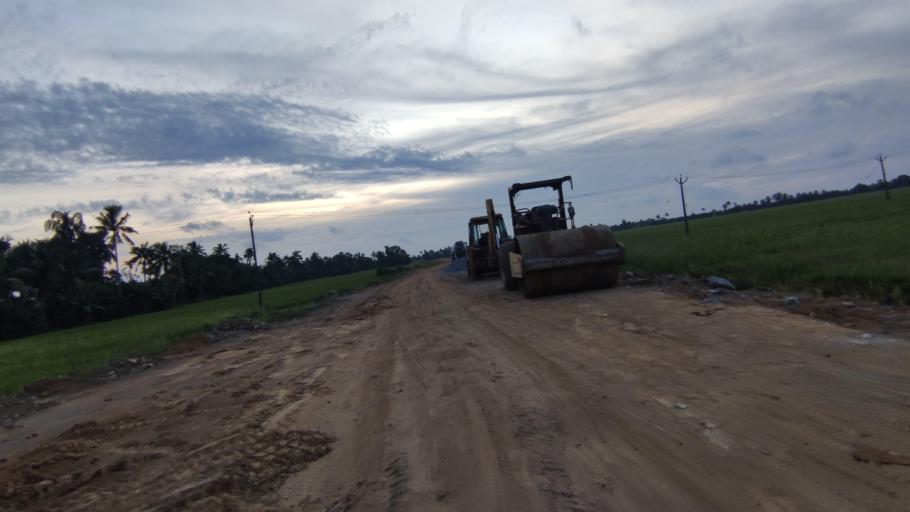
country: IN
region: Kerala
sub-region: Kottayam
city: Kottayam
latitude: 9.6470
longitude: 76.4641
